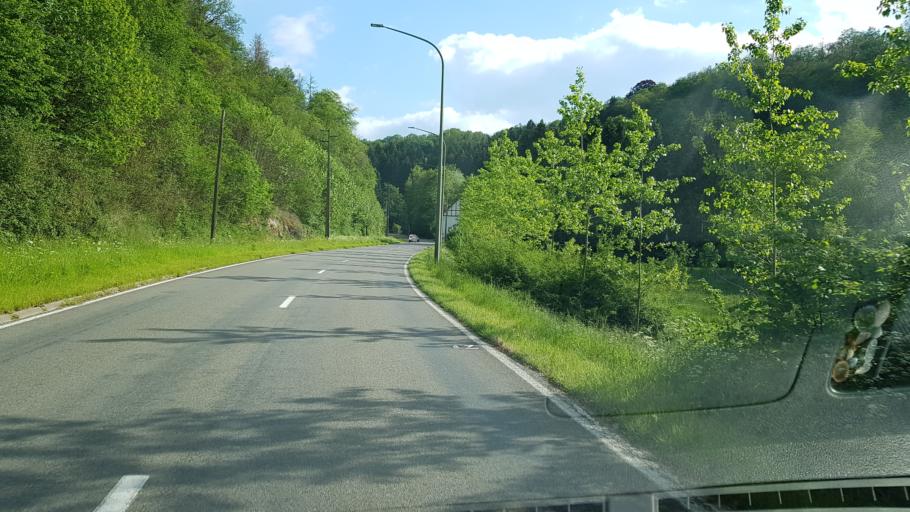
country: BE
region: Wallonia
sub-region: Province de Liege
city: Trooz
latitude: 50.5403
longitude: 5.6927
